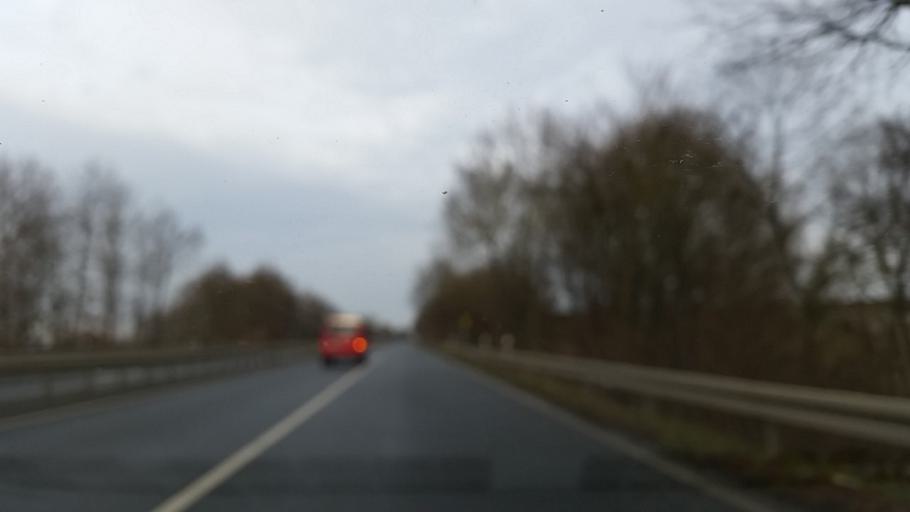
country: DE
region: Lower Saxony
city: Alt Wallmoden
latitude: 52.0265
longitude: 10.3539
